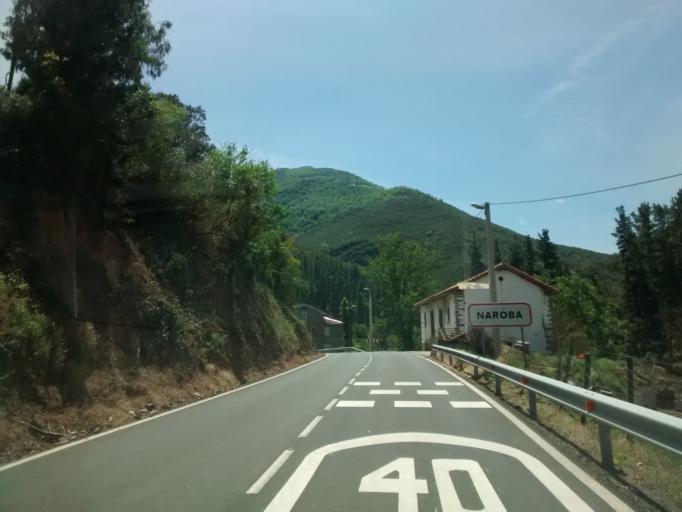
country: ES
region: Cantabria
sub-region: Provincia de Cantabria
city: Potes
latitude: 43.1221
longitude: -4.6292
